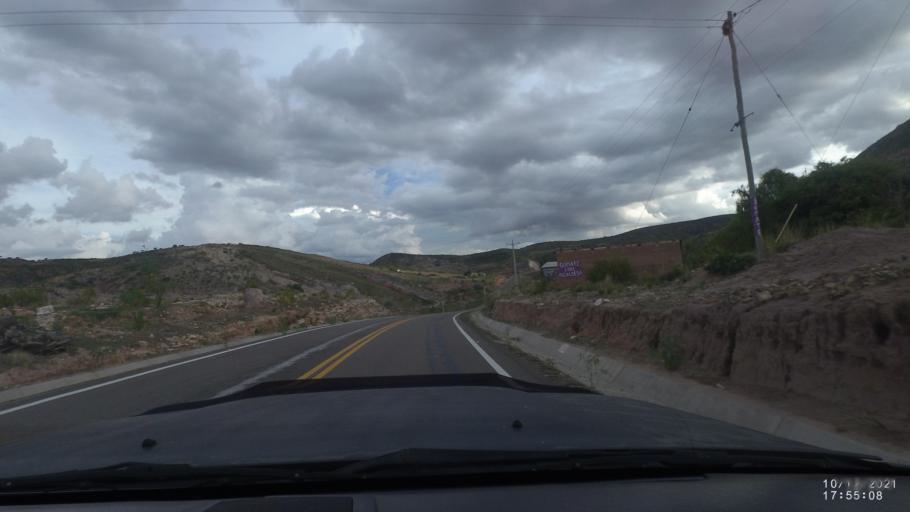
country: BO
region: Cochabamba
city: Cliza
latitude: -17.7067
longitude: -65.9438
